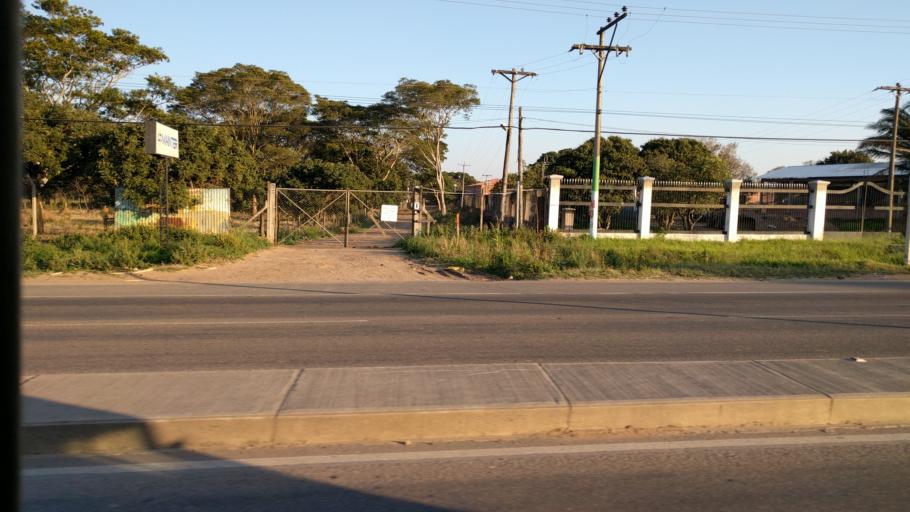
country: BO
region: Santa Cruz
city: Cotoca
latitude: -17.7632
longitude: -63.0292
